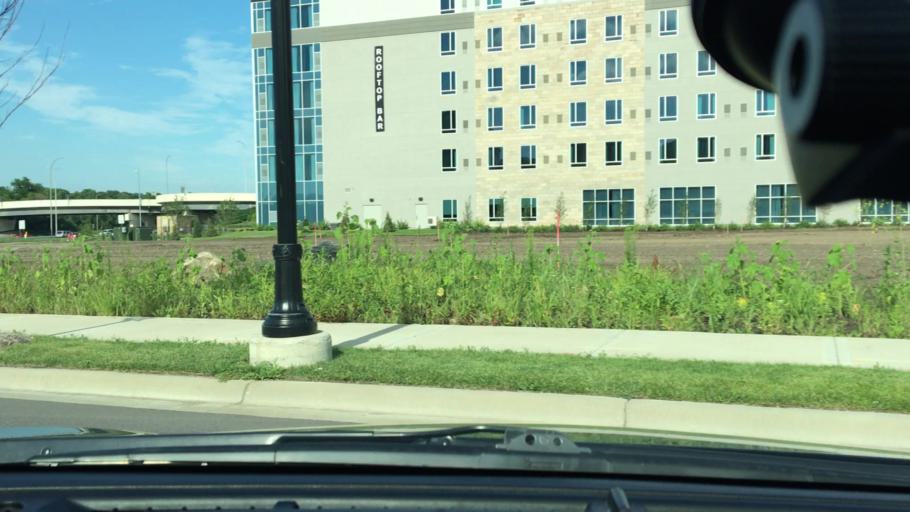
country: US
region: Minnesota
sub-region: Hennepin County
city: Saint Louis Park
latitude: 44.9694
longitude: -93.3453
